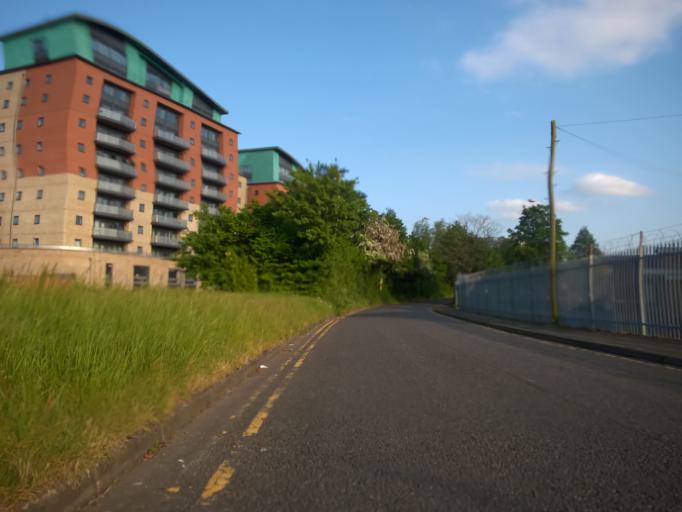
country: GB
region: England
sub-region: City of Leicester
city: Leicester
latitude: 52.6351
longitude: -1.1441
